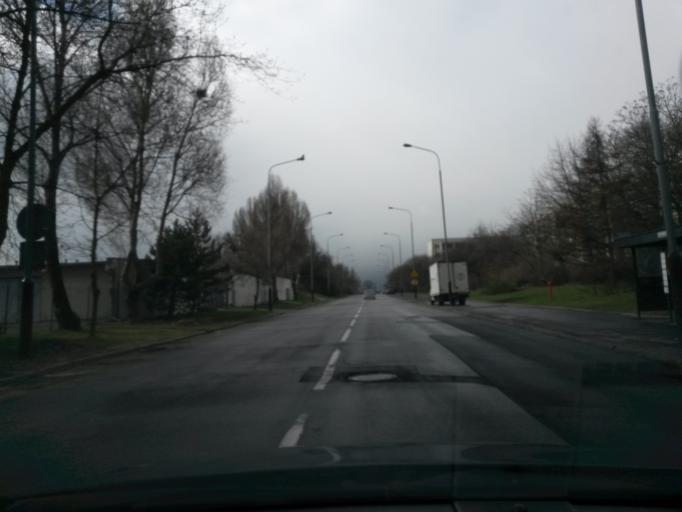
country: PL
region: Greater Poland Voivodeship
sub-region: Poznan
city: Poznan
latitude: 52.3870
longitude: 16.9712
